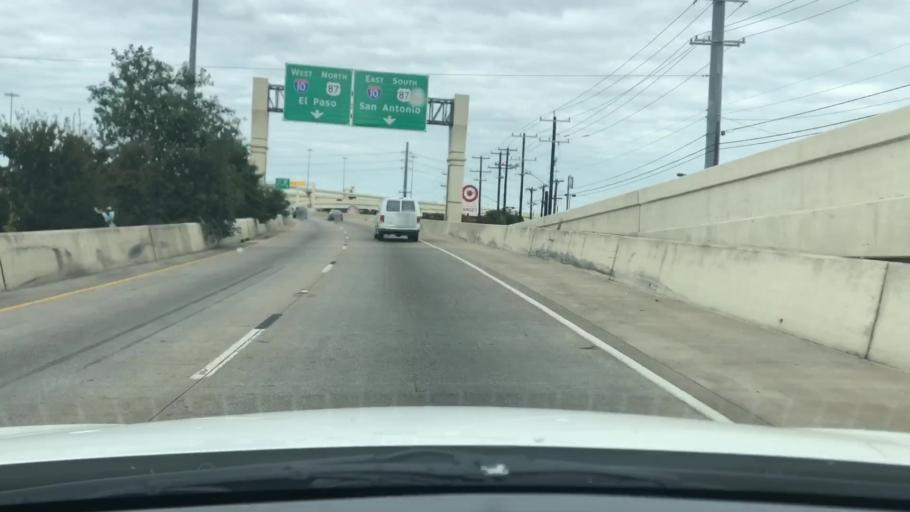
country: US
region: Texas
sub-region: Bexar County
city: Balcones Heights
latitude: 29.4946
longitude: -98.5531
